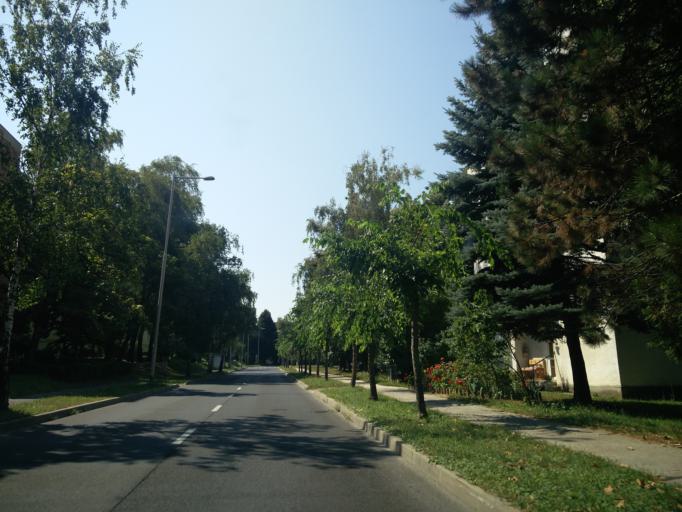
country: HU
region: Zala
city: Zalaegerszeg
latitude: 46.8270
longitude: 16.8373
